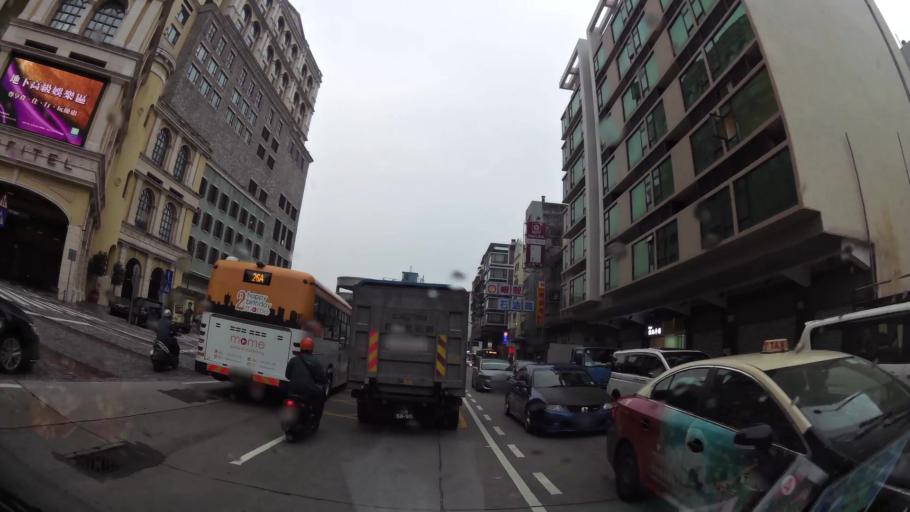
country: CN
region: Guangdong
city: Wanzai
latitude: 22.1970
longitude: 113.5366
